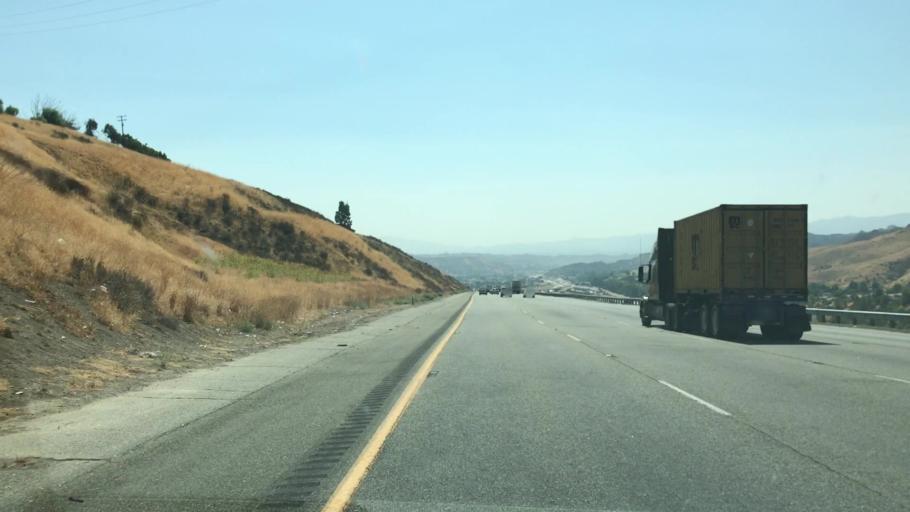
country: US
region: California
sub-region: Los Angeles County
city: Castaic
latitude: 34.5194
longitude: -118.6380
